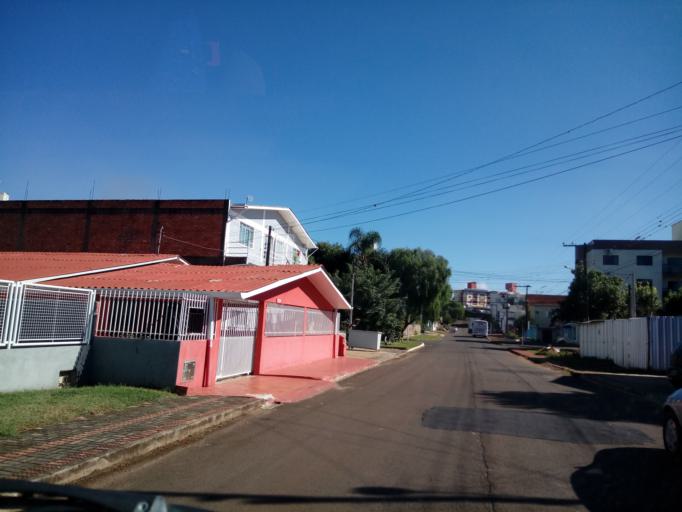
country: BR
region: Santa Catarina
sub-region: Chapeco
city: Chapeco
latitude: -27.0962
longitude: -52.6351
